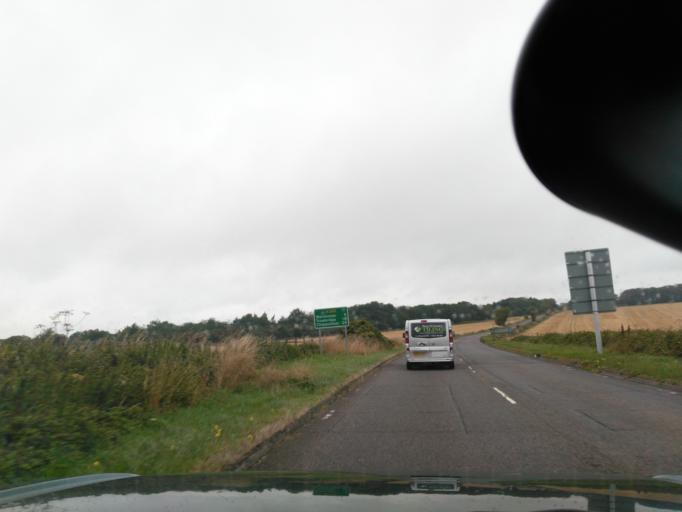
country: GB
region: England
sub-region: Wiltshire
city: Chicklade
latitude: 51.1082
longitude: -2.1684
